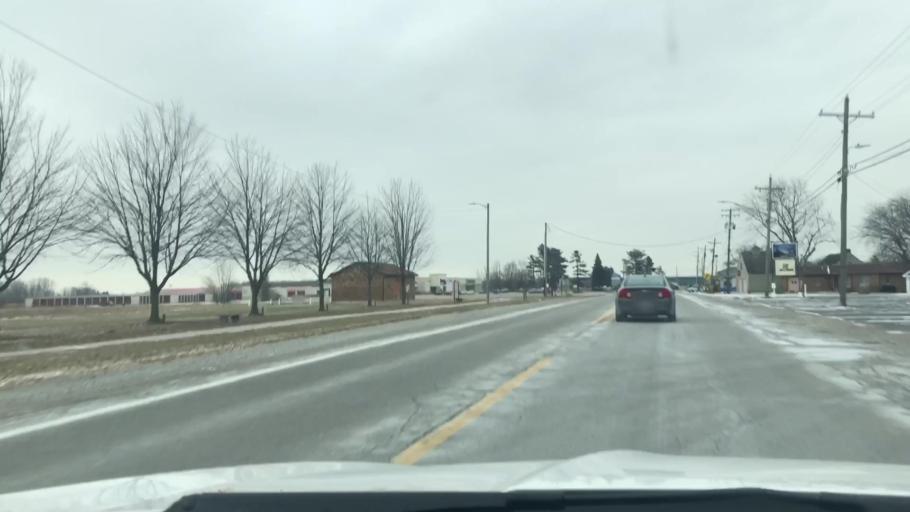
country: US
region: Indiana
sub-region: Fulton County
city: Rochester
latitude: 41.0619
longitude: -86.1859
